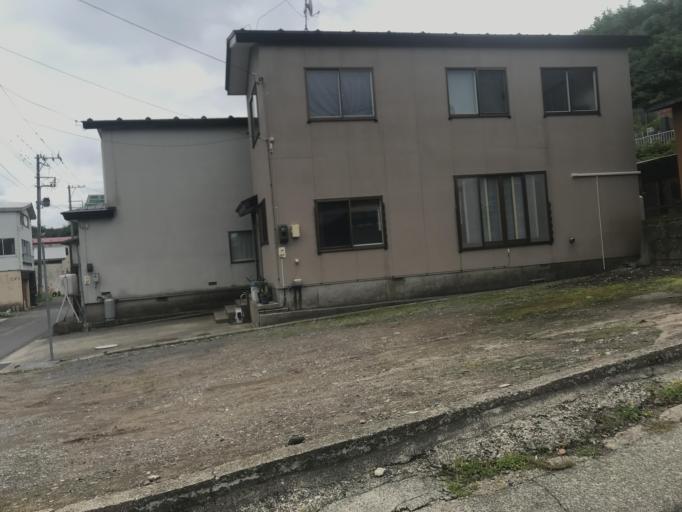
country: JP
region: Aomori
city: Shimokizukuri
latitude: 40.7831
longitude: 140.1969
